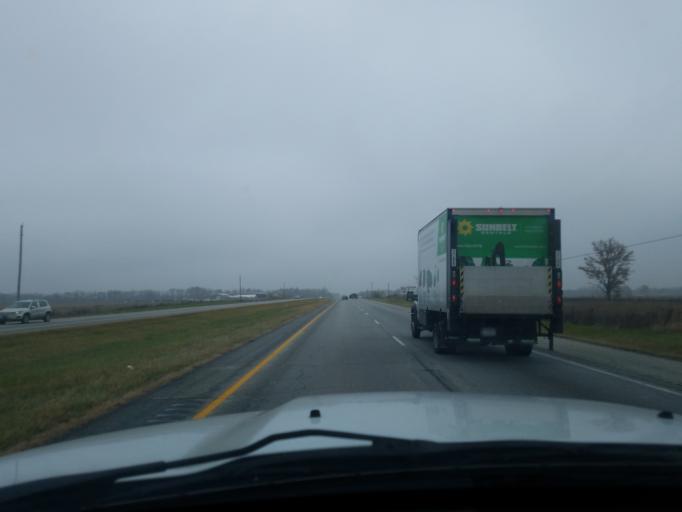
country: US
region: Indiana
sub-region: Hamilton County
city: Sheridan
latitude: 40.1815
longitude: -86.1280
